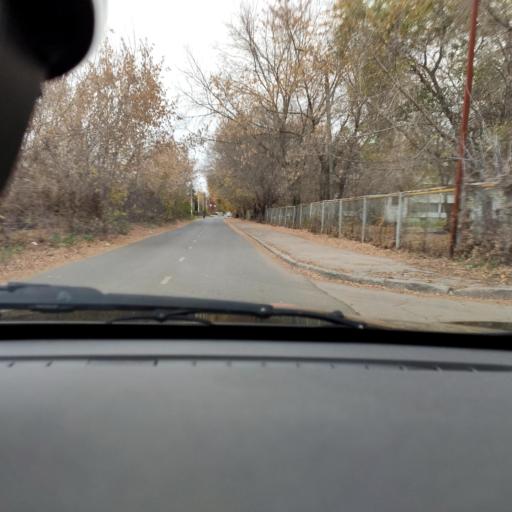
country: RU
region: Samara
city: Tol'yatti
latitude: 53.5280
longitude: 49.3913
